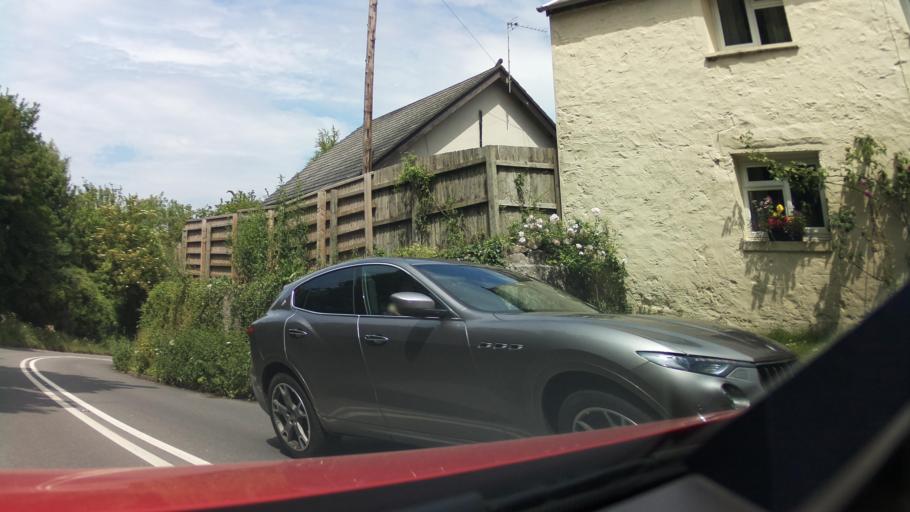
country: GB
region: Wales
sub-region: Vale of Glamorgan
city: Rhoose
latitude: 51.3989
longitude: -3.3895
